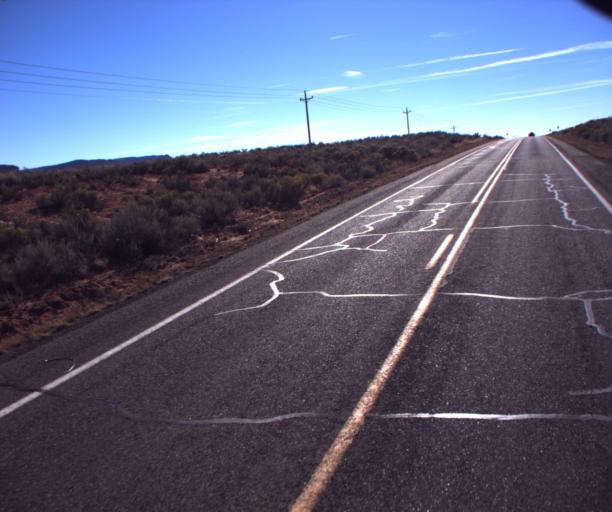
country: US
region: Arizona
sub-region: Mohave County
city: Colorado City
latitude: 36.9162
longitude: -112.9319
